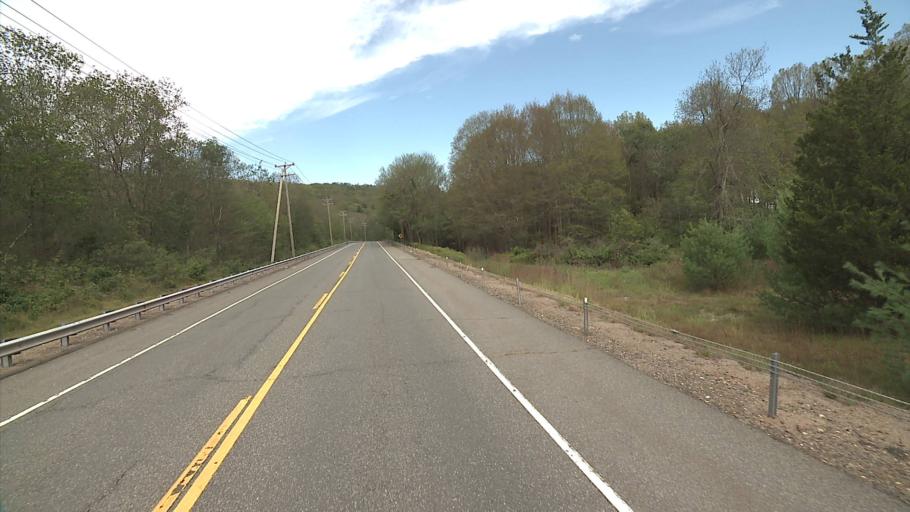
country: US
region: Connecticut
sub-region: Tolland County
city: Stafford Springs
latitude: 41.9105
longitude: -72.2941
